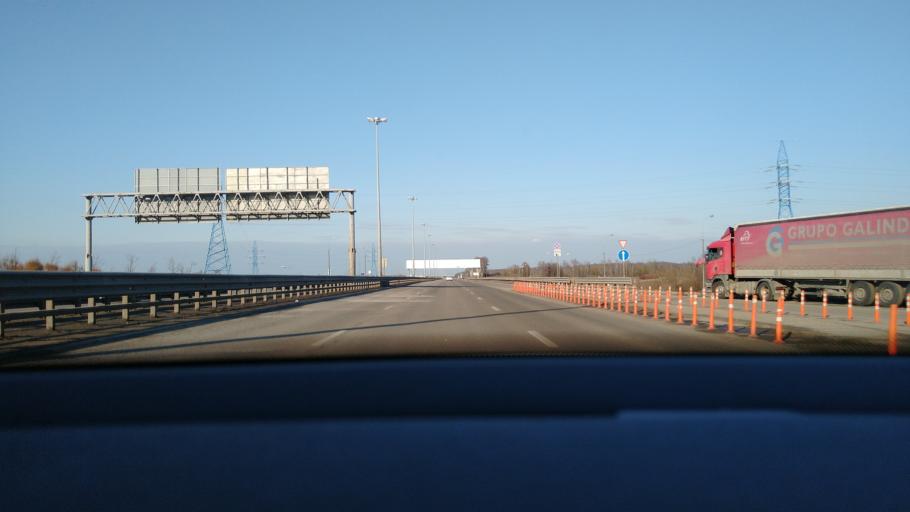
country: RU
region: Moscow
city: Khimki
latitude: 55.9269
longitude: 37.3979
